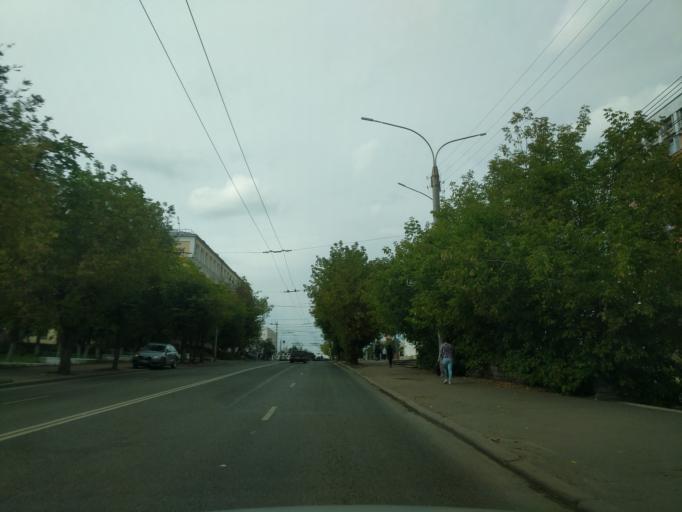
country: RU
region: Kirov
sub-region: Kirovo-Chepetskiy Rayon
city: Kirov
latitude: 58.5925
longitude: 49.6688
